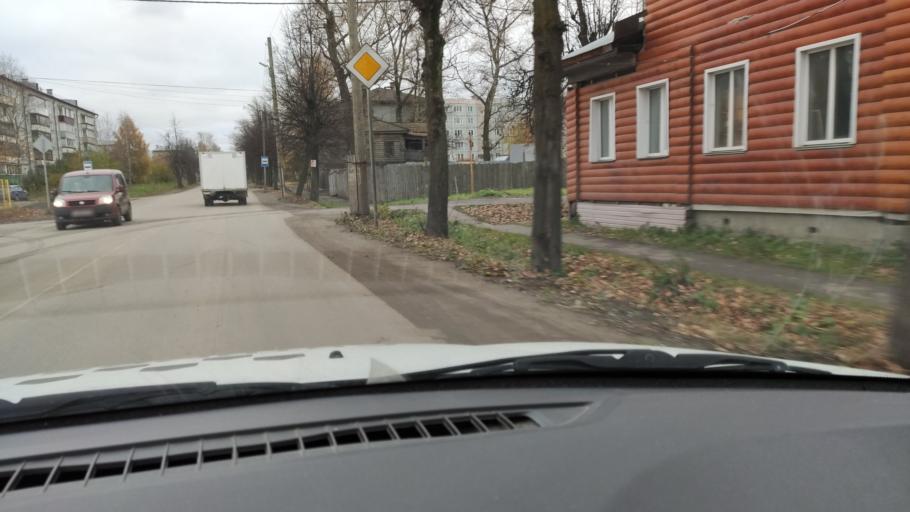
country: RU
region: Kirov
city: Slobodskoy
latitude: 58.7288
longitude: 50.1741
